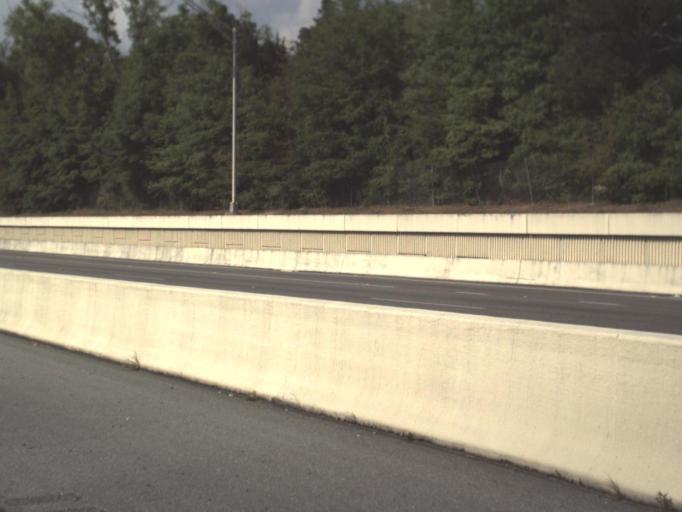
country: US
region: Florida
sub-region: Escambia County
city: Brent
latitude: 30.4761
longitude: -87.2292
